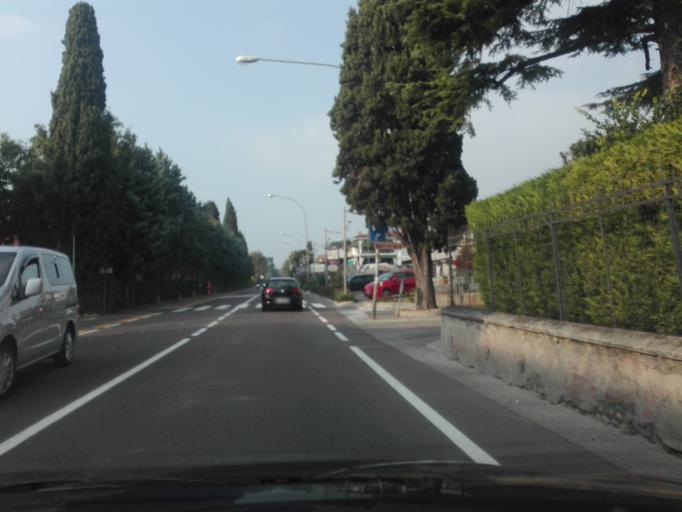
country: IT
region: Veneto
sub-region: Provincia di Verona
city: Lazise
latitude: 45.5083
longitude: 10.7343
